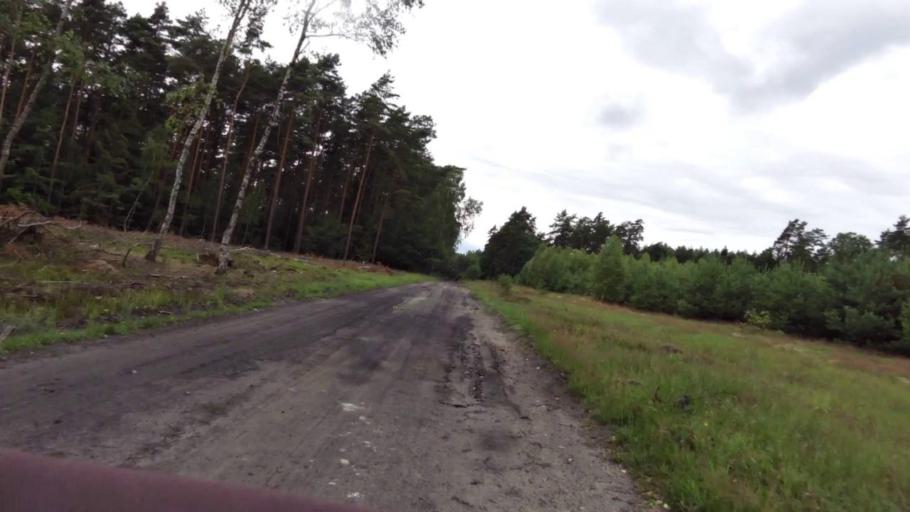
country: PL
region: West Pomeranian Voivodeship
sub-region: Powiat mysliborski
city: Debno
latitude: 52.8099
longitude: 14.6696
